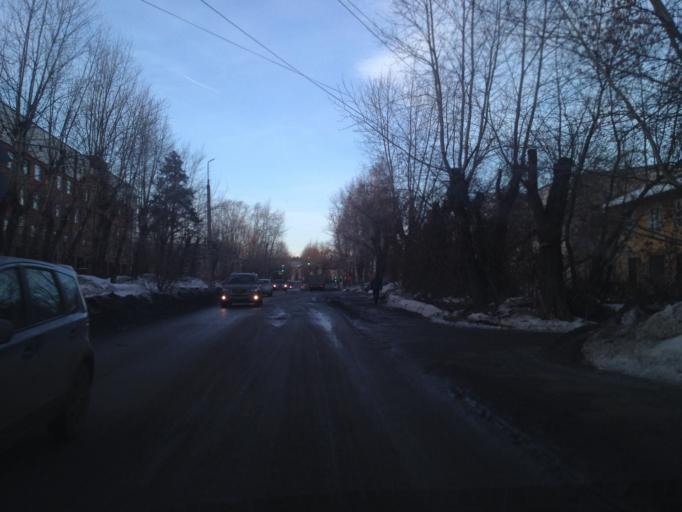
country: RU
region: Sverdlovsk
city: Istok
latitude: 56.7572
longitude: 60.7105
